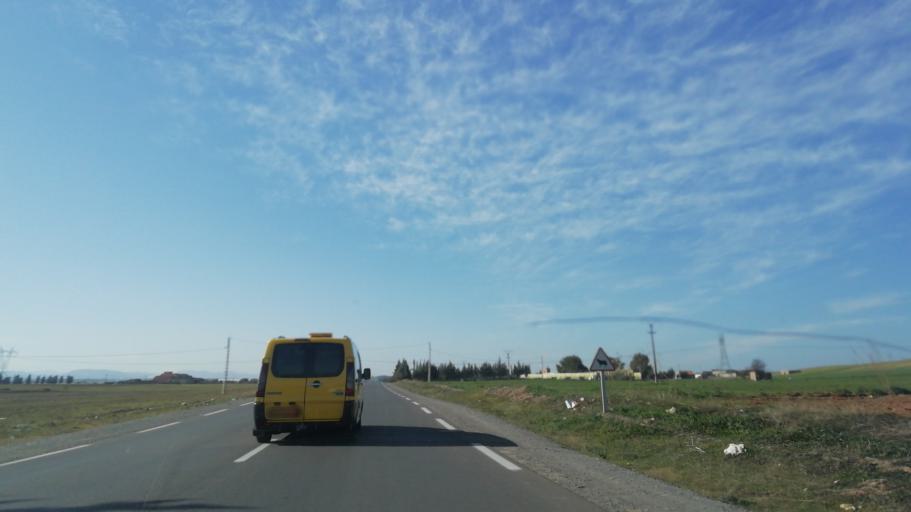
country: DZ
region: Tlemcen
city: Ouled Mimoun
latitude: 35.0442
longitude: -0.8415
